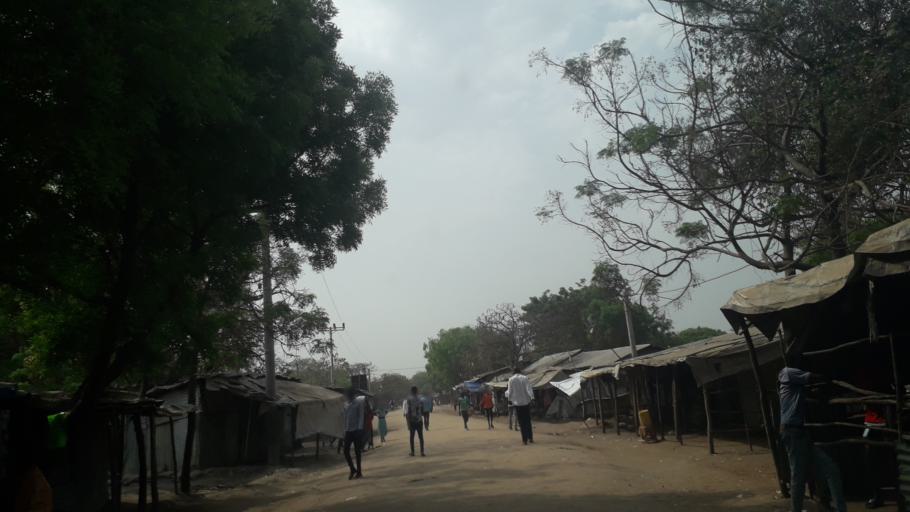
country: ET
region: Gambela
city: Gambela
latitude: 8.3025
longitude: 33.6832
